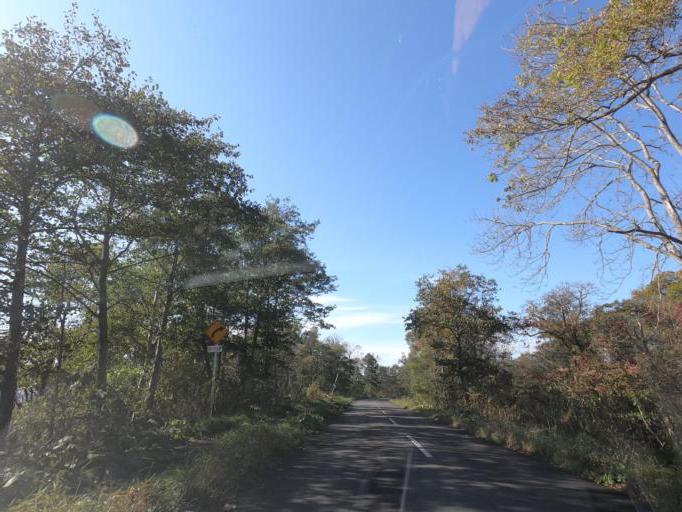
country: JP
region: Hokkaido
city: Obihiro
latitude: 42.6090
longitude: 143.5465
